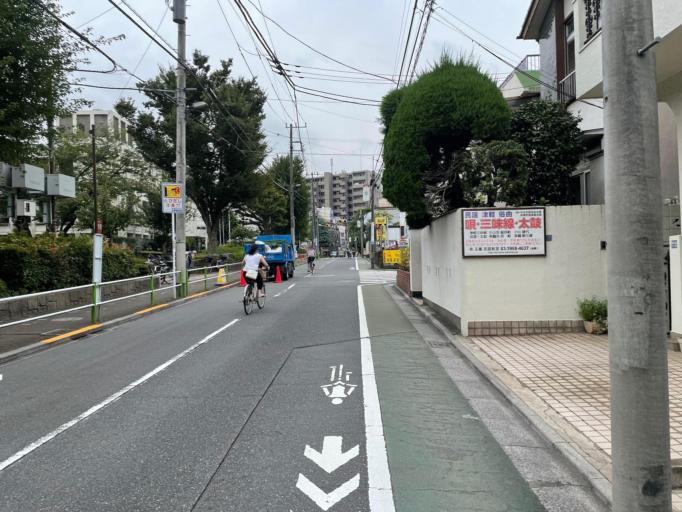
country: JP
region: Saitama
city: Kawaguchi
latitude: 35.7607
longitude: 139.6915
